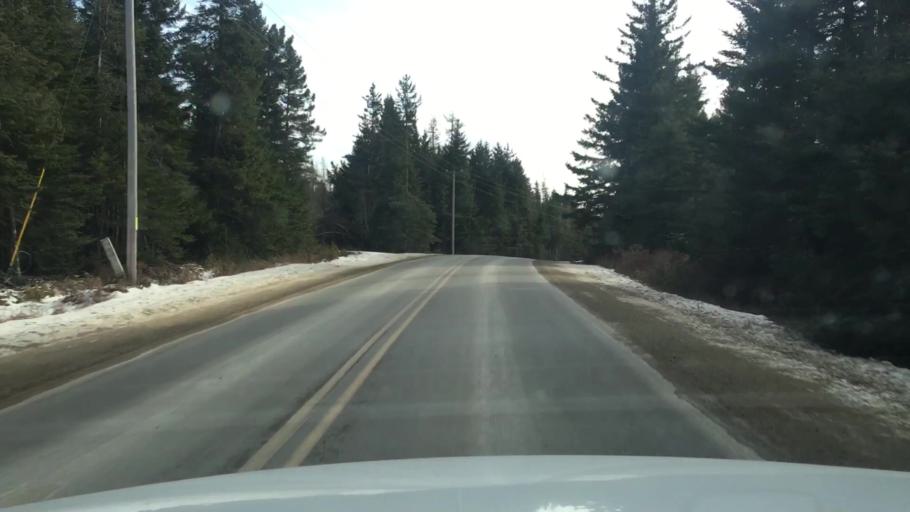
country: US
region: Maine
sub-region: Washington County
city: Jonesport
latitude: 44.6372
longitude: -67.5932
